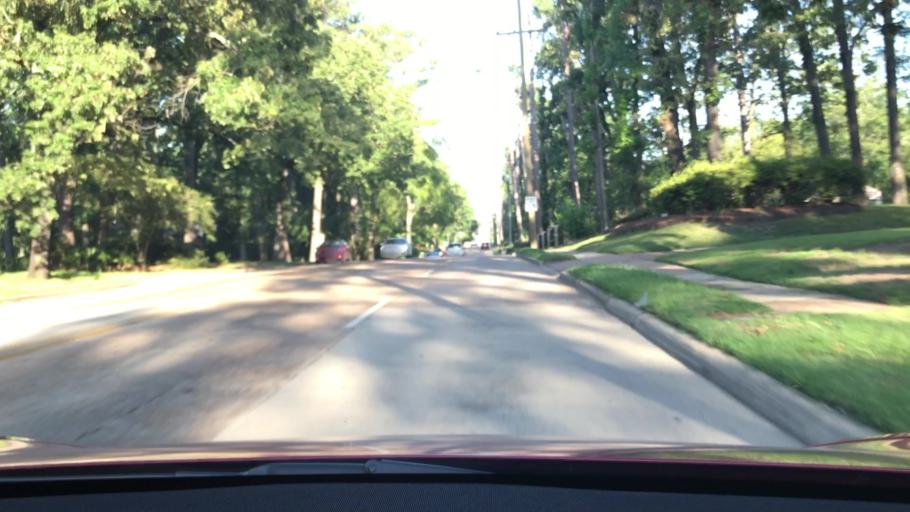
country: US
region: Louisiana
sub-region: Bossier Parish
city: Bossier City
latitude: 32.4547
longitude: -93.7385
